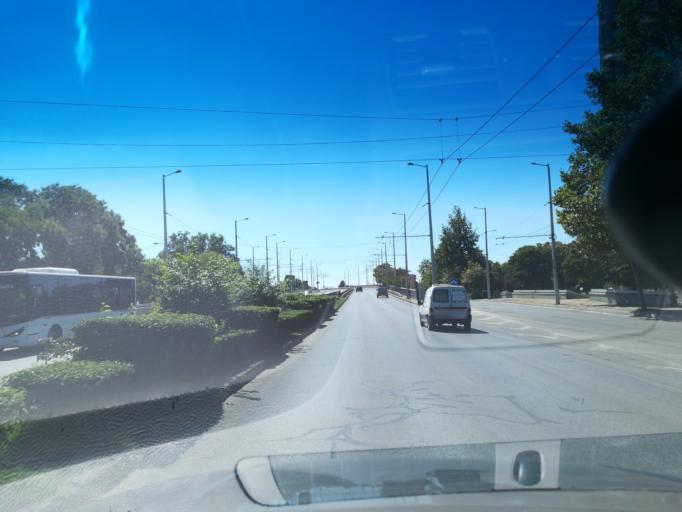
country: BG
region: Plovdiv
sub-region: Obshtina Plovdiv
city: Plovdiv
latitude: 42.1345
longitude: 24.7598
